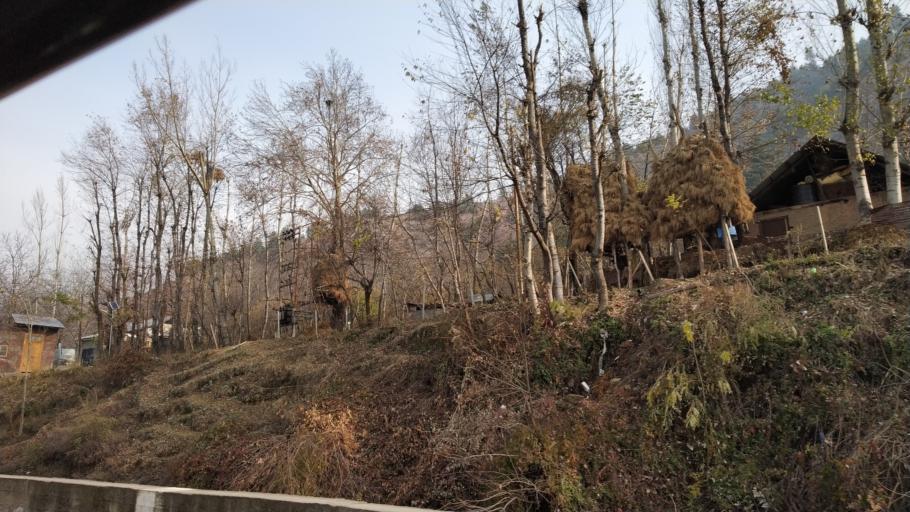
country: IN
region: Kashmir
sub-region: Anantnag
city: Pahalgam
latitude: 33.8691
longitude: 75.2785
